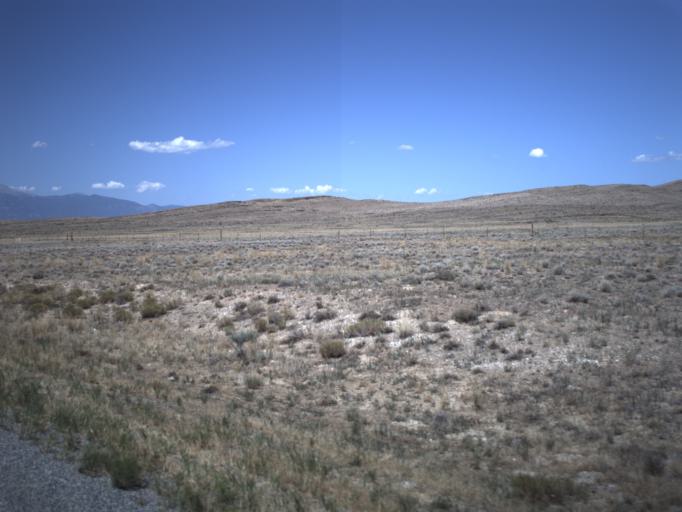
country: US
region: Utah
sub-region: Beaver County
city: Milford
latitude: 39.0447
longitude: -113.8004
